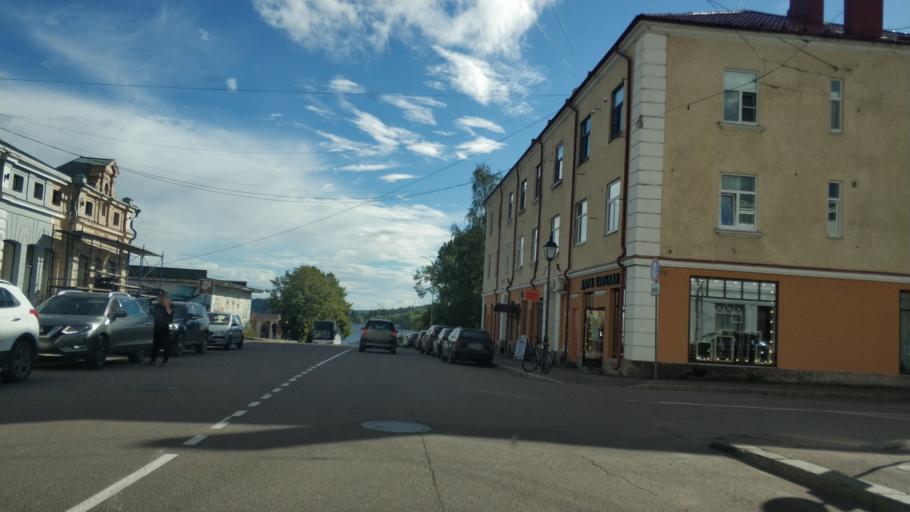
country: RU
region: Republic of Karelia
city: Sortavala
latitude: 61.7014
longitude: 30.6916
